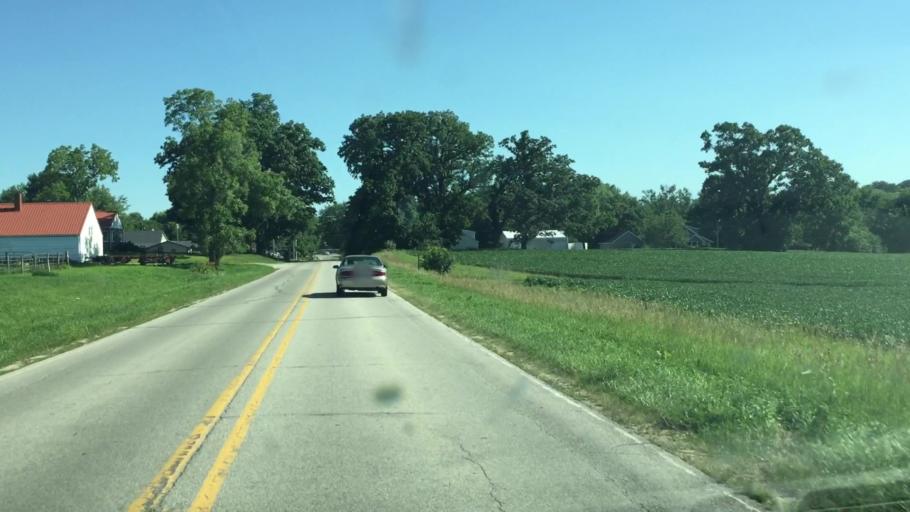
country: US
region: Iowa
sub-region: Linn County
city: Ely
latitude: 41.8526
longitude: -91.6462
